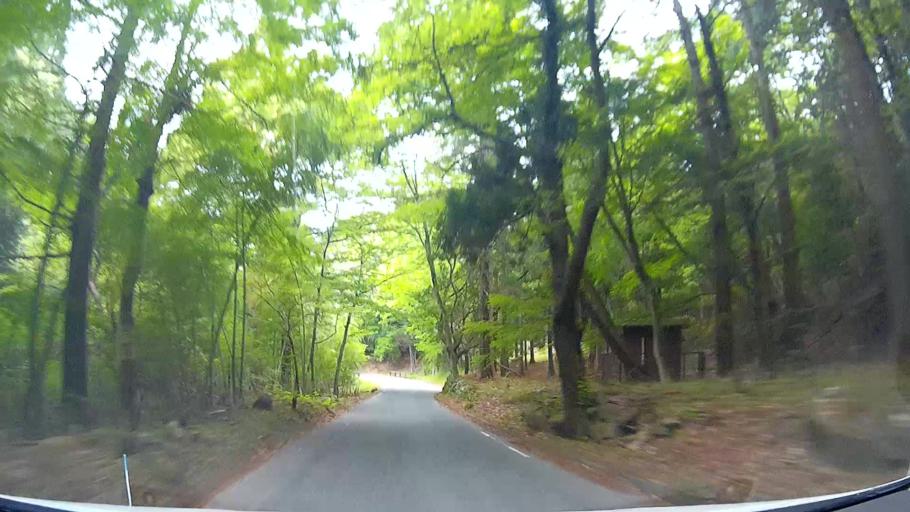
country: JP
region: Shizuoka
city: Ito
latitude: 34.9131
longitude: 139.0506
